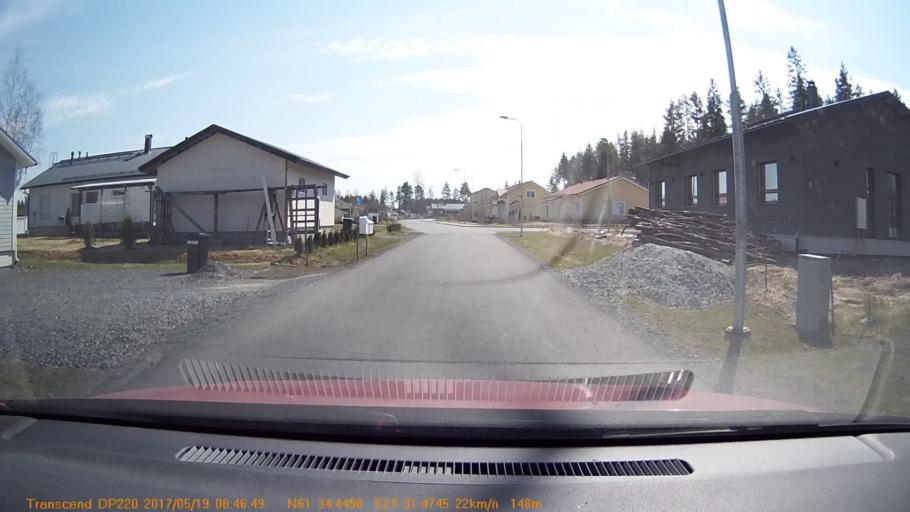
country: FI
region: Pirkanmaa
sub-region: Tampere
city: Yloejaervi
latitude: 61.5742
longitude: 23.5244
